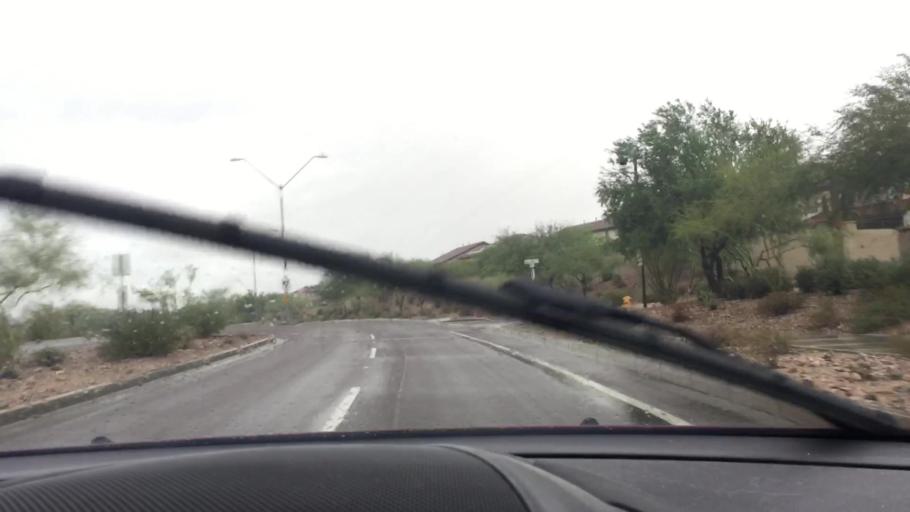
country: US
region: Arizona
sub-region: Maricopa County
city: Sun City West
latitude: 33.7348
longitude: -112.2538
